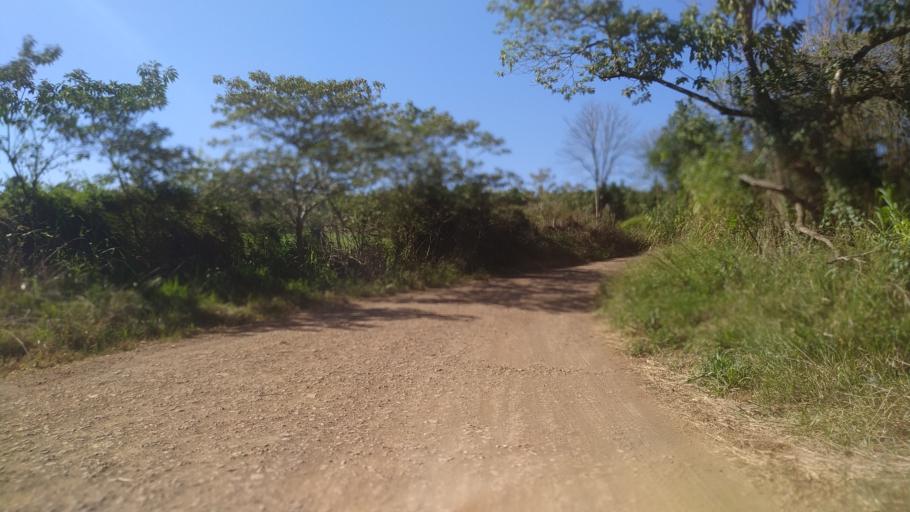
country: BR
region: Santa Catarina
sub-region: Chapeco
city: Chapeco
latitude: -27.1493
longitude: -52.6048
